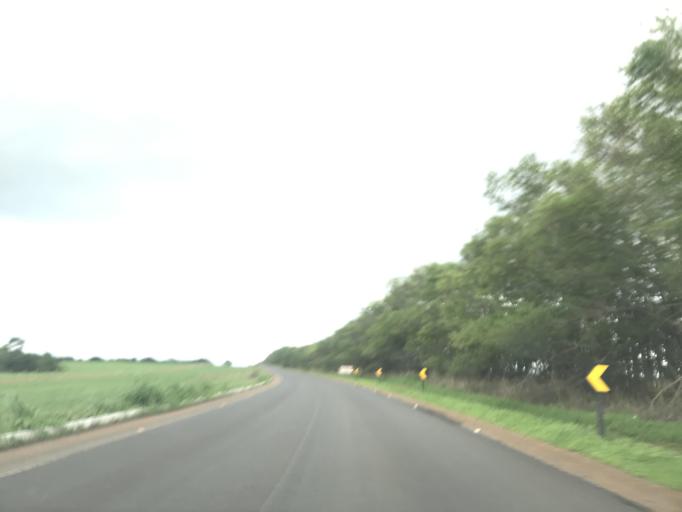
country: BR
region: Goias
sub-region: Vianopolis
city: Vianopolis
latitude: -16.8071
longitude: -48.5185
